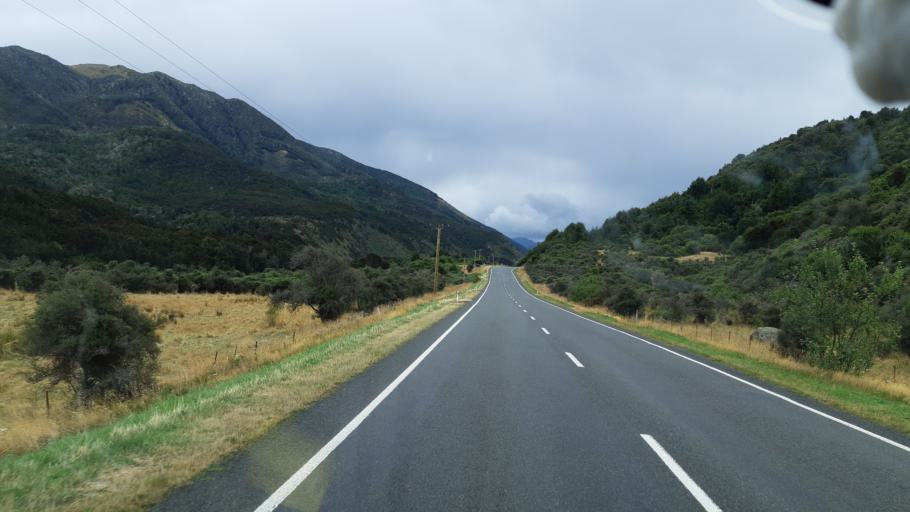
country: NZ
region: Canterbury
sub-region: Hurunui District
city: Amberley
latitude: -42.5728
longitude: 172.3698
